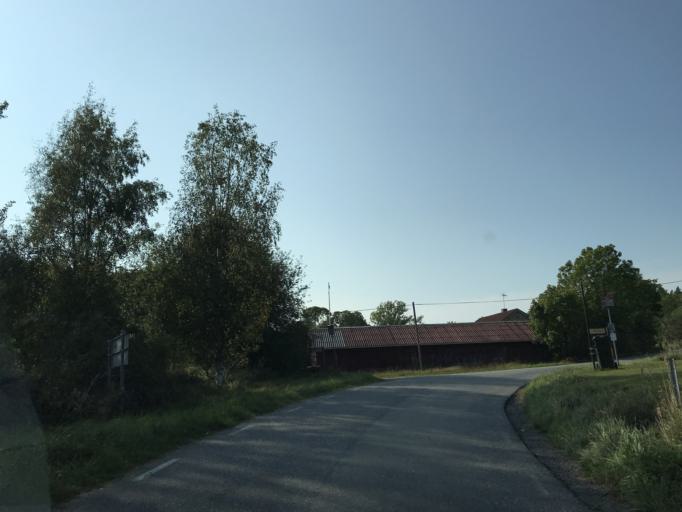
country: SE
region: Stockholm
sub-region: Norrtalje Kommun
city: Bjorko
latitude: 59.8715
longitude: 19.0688
